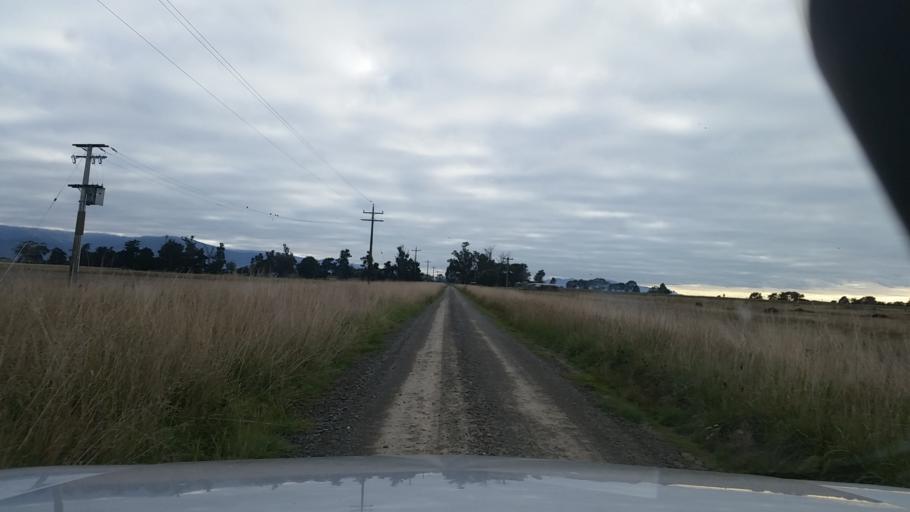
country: NZ
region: Marlborough
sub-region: Marlborough District
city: Blenheim
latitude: -41.5043
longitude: 174.0317
